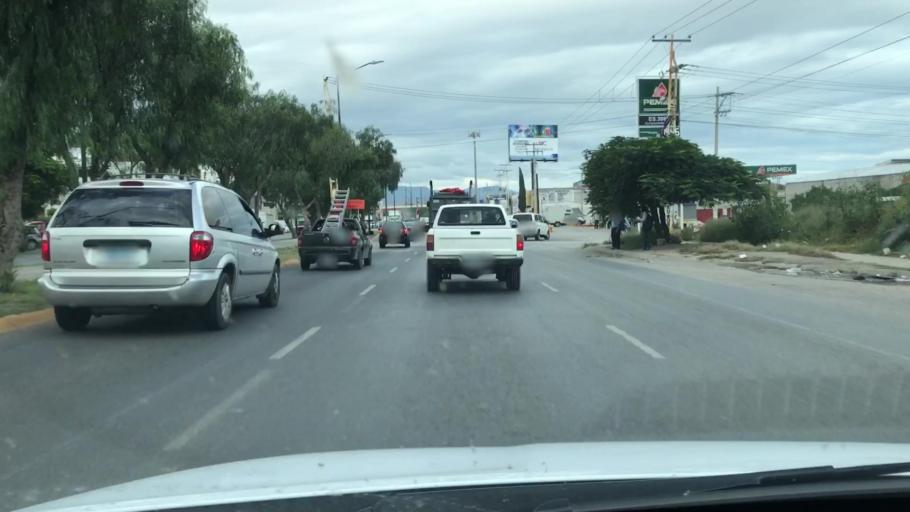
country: MX
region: Guanajuato
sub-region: Leon
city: Centro Familiar la Soledad
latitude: 21.0969
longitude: -101.7256
